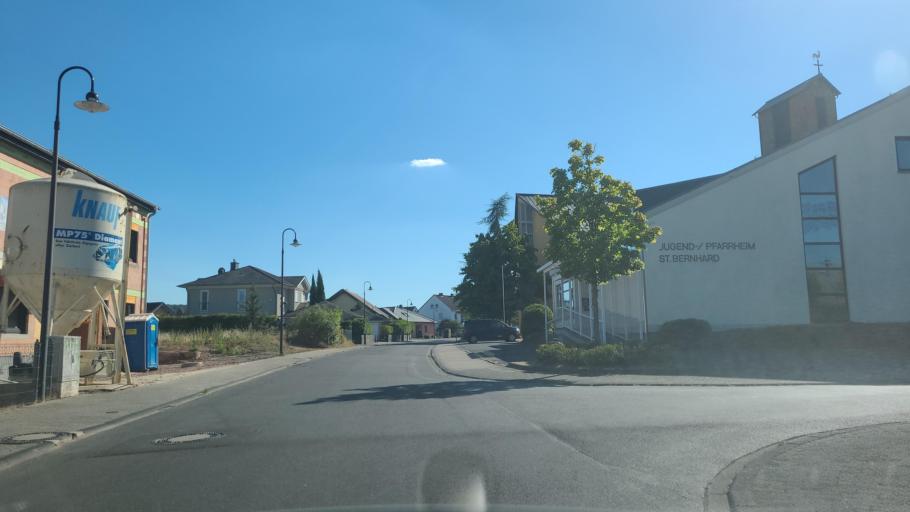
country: DE
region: Rheinland-Pfalz
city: Wittlich
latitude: 49.9812
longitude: 6.8866
